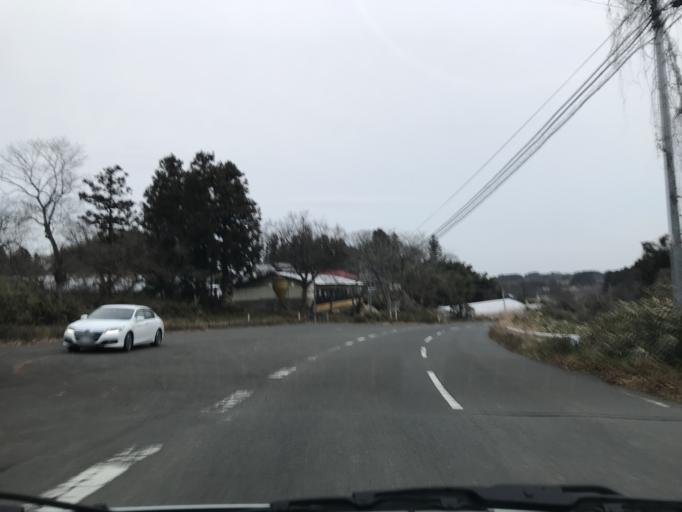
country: JP
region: Miyagi
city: Kogota
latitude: 38.6999
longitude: 141.0961
